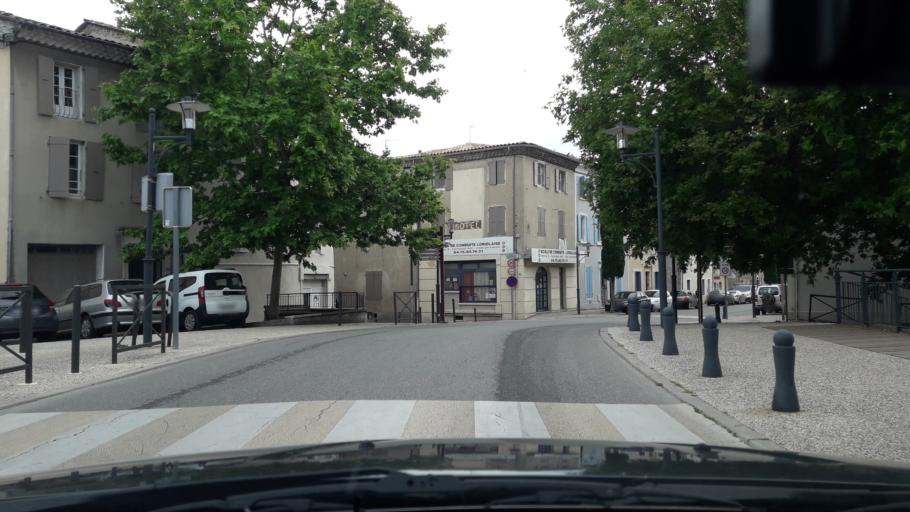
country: FR
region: Rhone-Alpes
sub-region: Departement de la Drome
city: Loriol-sur-Drome
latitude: 44.7531
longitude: 4.8233
